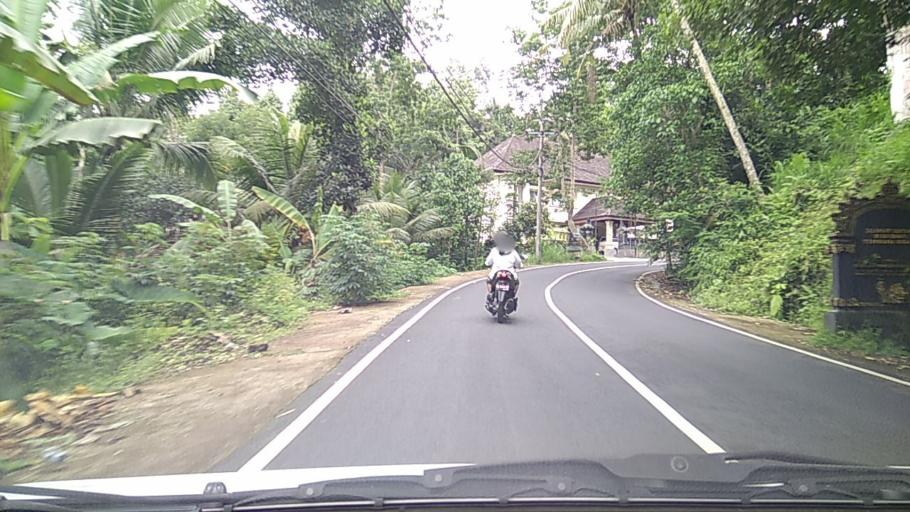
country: ID
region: Bali
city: Bangli
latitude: -8.4518
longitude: 115.3832
